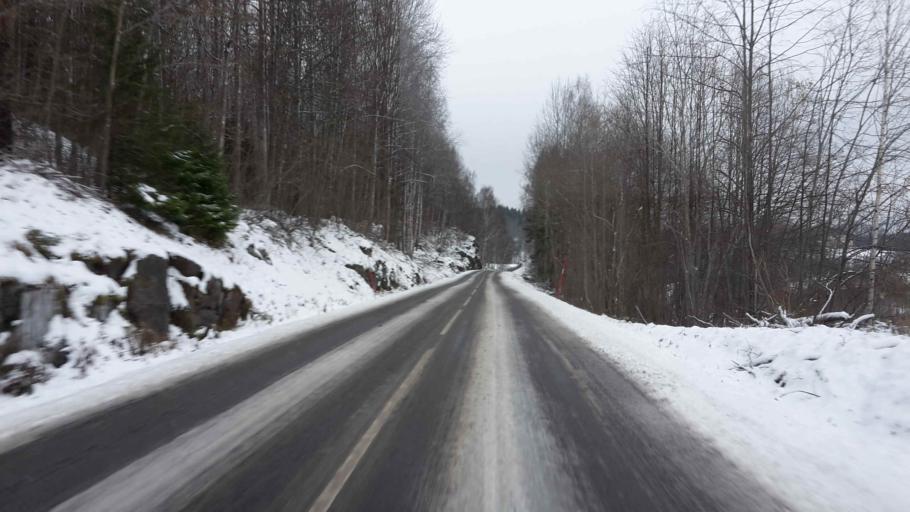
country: SE
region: OEstergoetland
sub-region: Atvidabergs Kommun
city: Atvidaberg
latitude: 58.1577
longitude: 16.1549
